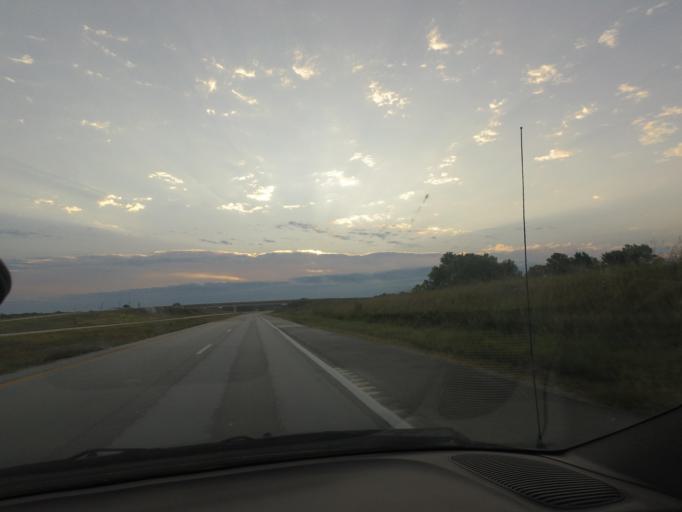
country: US
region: Missouri
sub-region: Macon County
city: Macon
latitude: 39.7519
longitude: -92.2610
